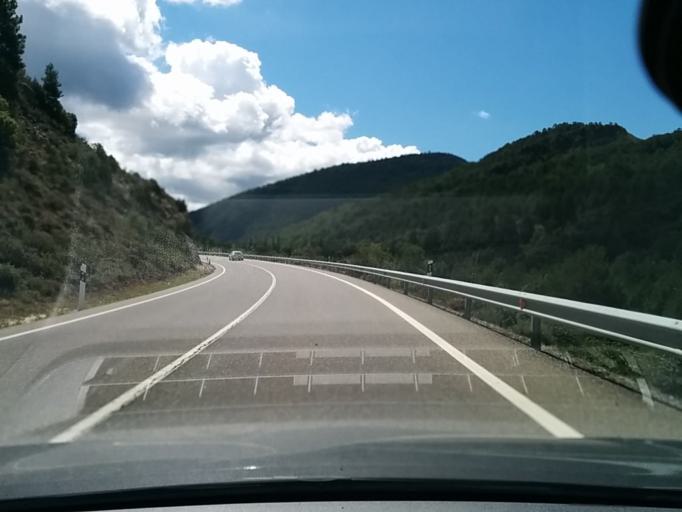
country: ES
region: Aragon
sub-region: Provincia de Huesca
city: Boltana
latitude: 42.4584
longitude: 0.0510
